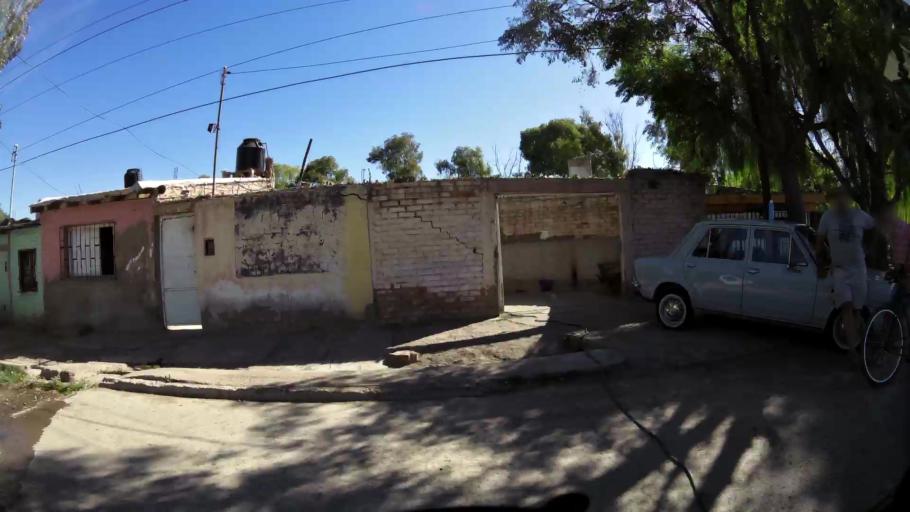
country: AR
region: Mendoza
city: Las Heras
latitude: -32.8391
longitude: -68.8044
